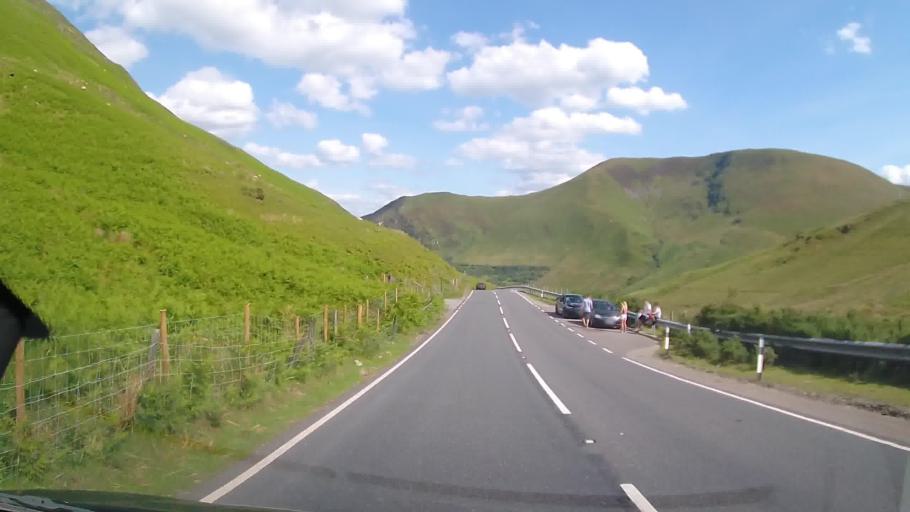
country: GB
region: Wales
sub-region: Gwynedd
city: Corris
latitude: 52.7358
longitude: -3.7678
